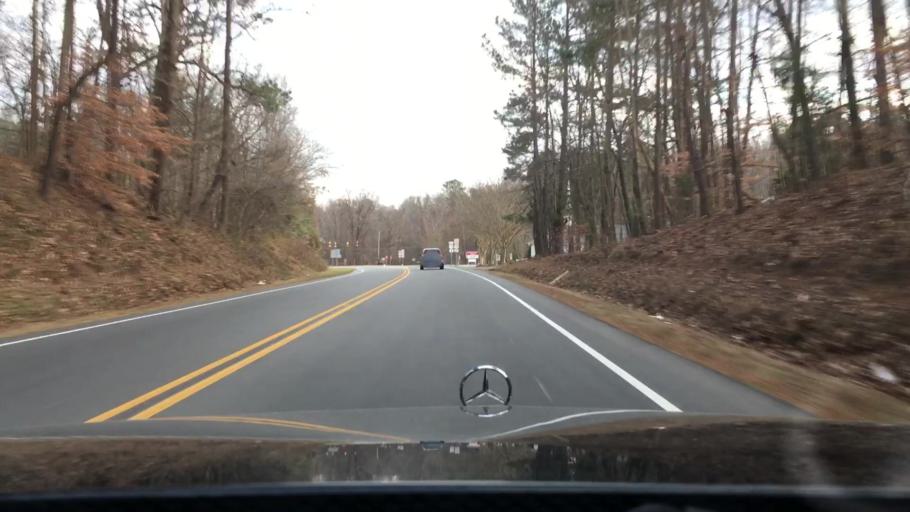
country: US
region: North Carolina
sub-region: Orange County
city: Hillsborough
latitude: 36.0577
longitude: -79.0514
